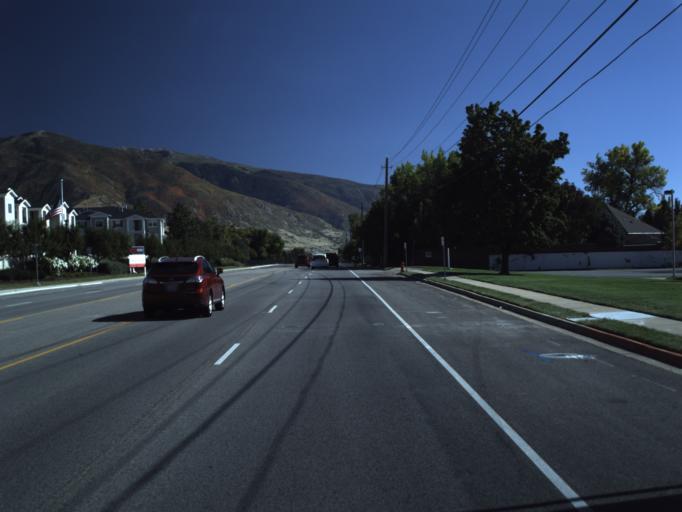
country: US
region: Utah
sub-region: Davis County
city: Kaysville
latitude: 41.0215
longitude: -111.9248
